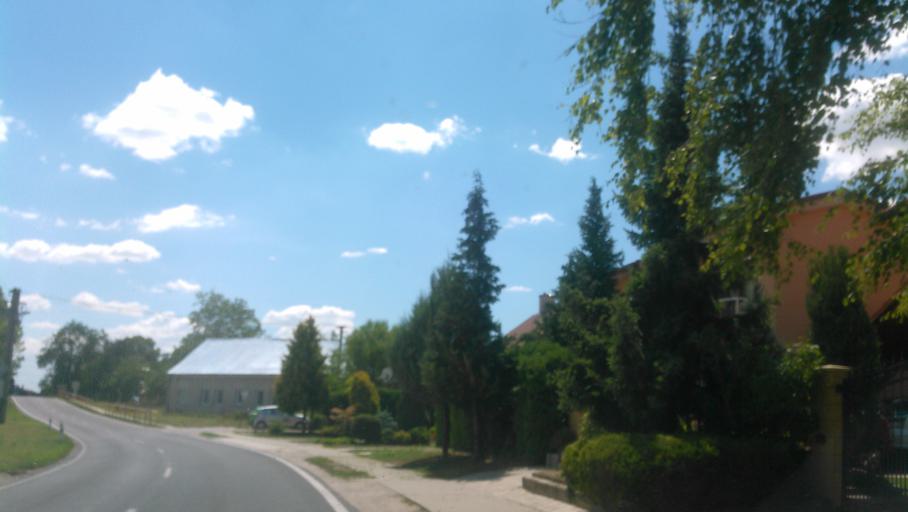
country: SK
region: Trnavsky
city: Vrbove
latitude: 48.5641
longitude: 17.7397
